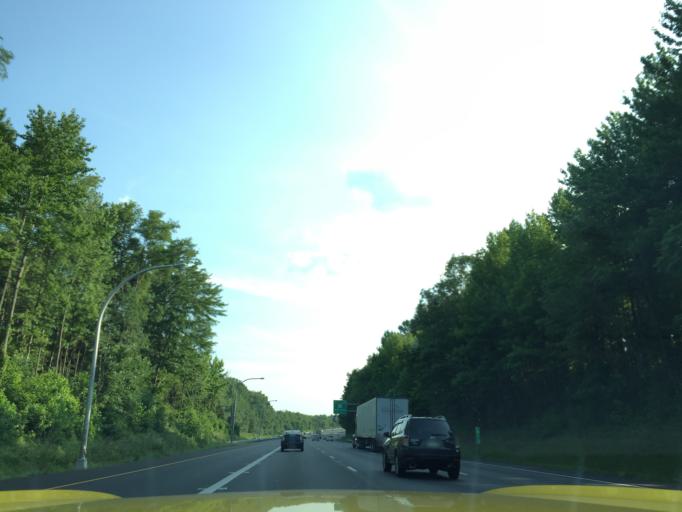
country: US
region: Maryland
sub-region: Harford County
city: Riverside
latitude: 39.4934
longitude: -76.2378
